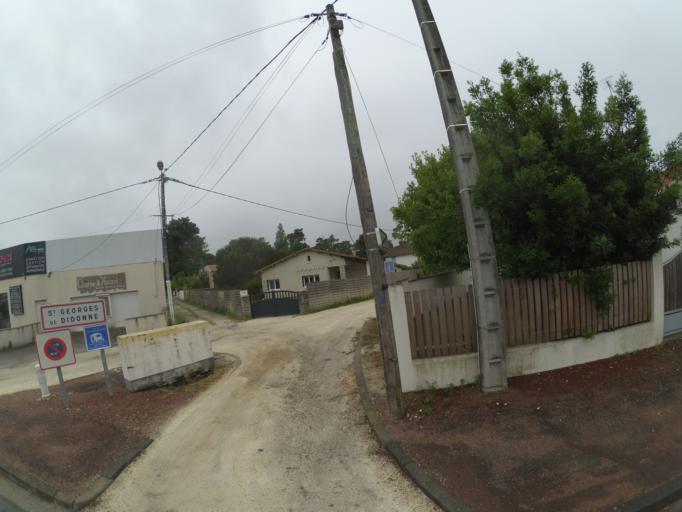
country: FR
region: Poitou-Charentes
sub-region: Departement de la Charente-Maritime
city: Saint-Georges-de-Didonne
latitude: 45.6139
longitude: -1.0000
